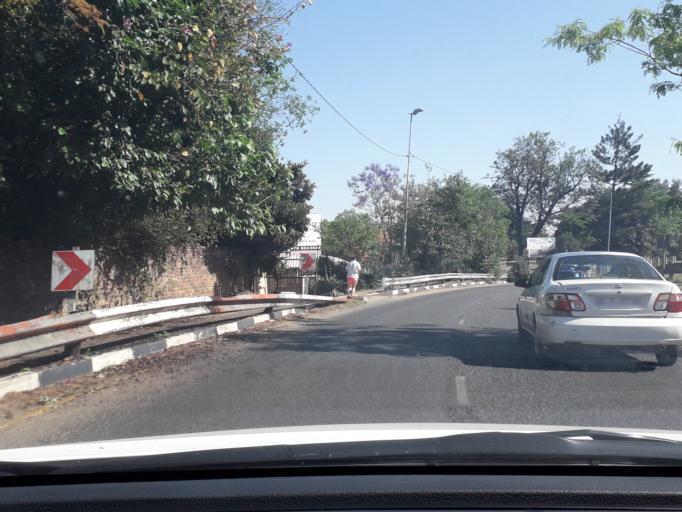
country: ZA
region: Gauteng
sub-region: City of Johannesburg Metropolitan Municipality
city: Roodepoort
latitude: -26.1156
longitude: 27.9720
